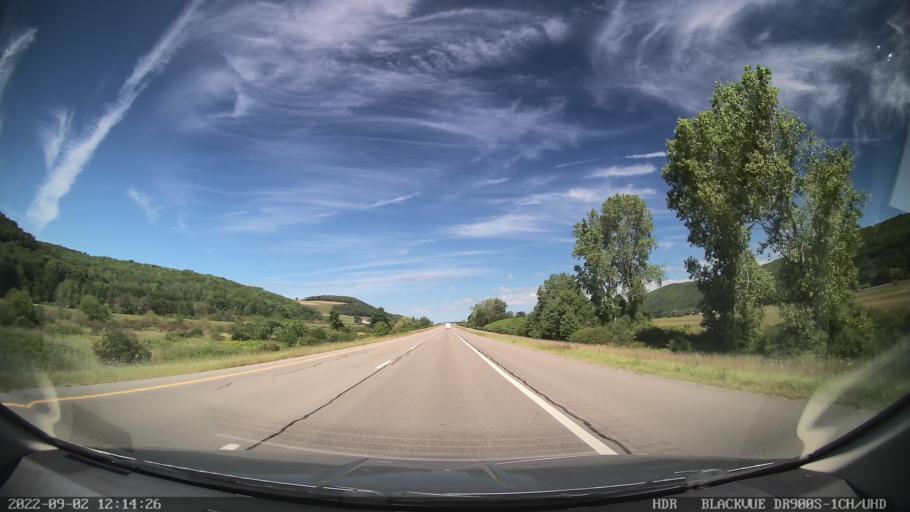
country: US
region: New York
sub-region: Steuben County
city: Wayland
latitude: 42.4522
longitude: -77.4759
